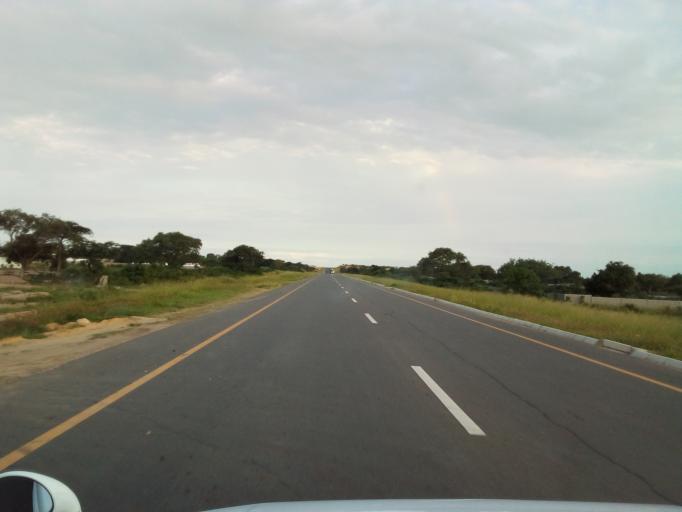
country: MZ
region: Maputo City
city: Maputo
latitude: -26.0376
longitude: 32.5582
